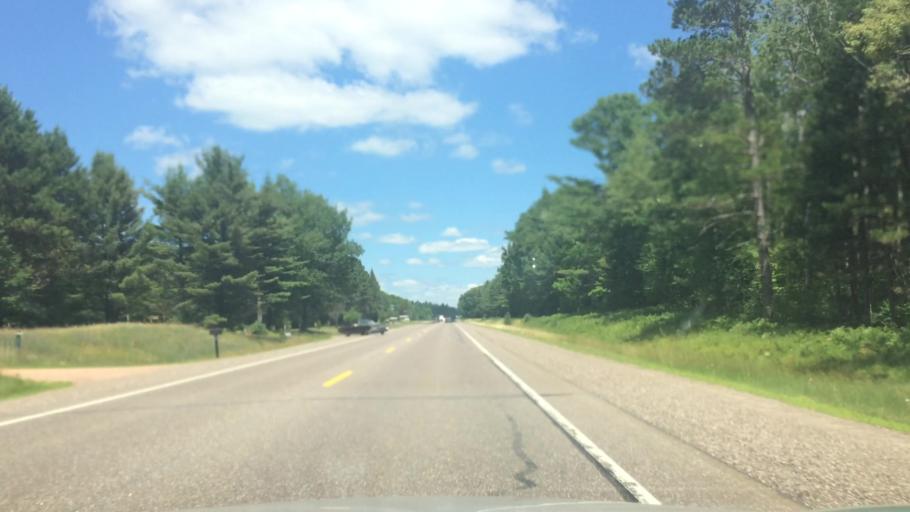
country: US
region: Wisconsin
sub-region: Vilas County
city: Lac du Flambeau
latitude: 45.9738
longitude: -89.6994
